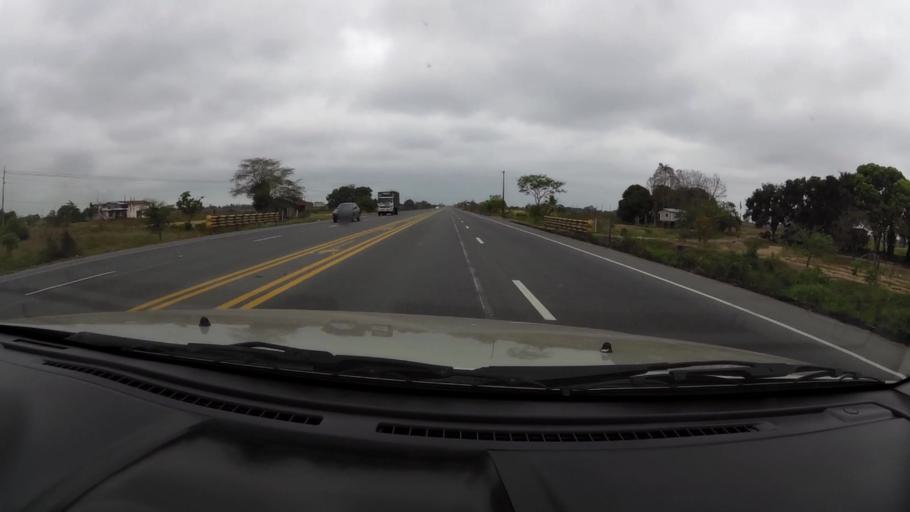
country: EC
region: Guayas
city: Naranjal
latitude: -2.4619
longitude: -79.6254
